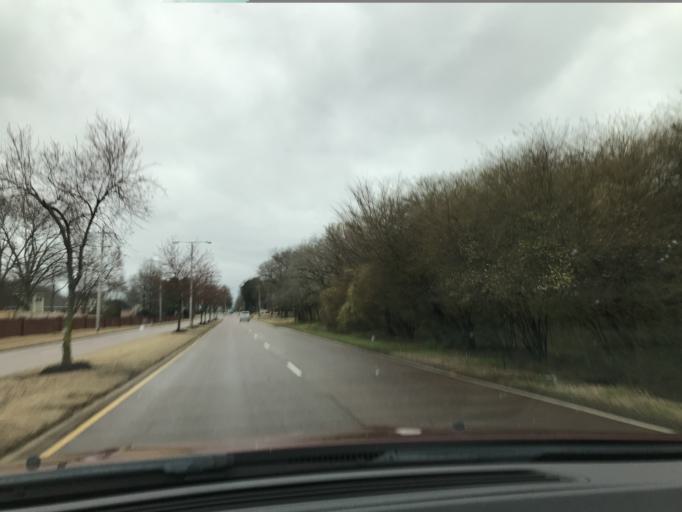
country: US
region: Tennessee
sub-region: Shelby County
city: Collierville
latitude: 35.0609
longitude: -89.6860
